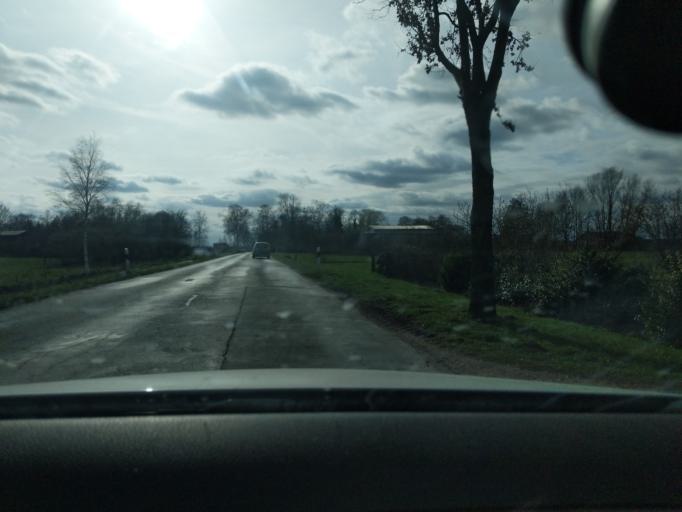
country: DE
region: Lower Saxony
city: Hammah
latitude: 53.6552
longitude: 9.3720
